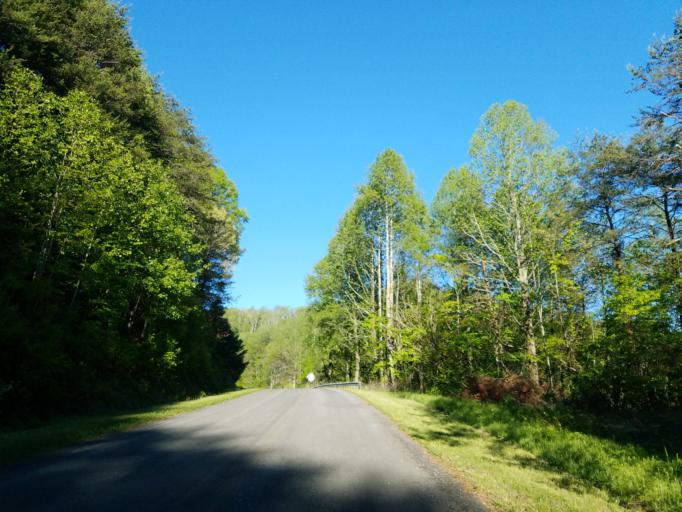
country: US
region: Georgia
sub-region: Fannin County
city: Blue Ridge
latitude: 34.7227
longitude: -84.2843
